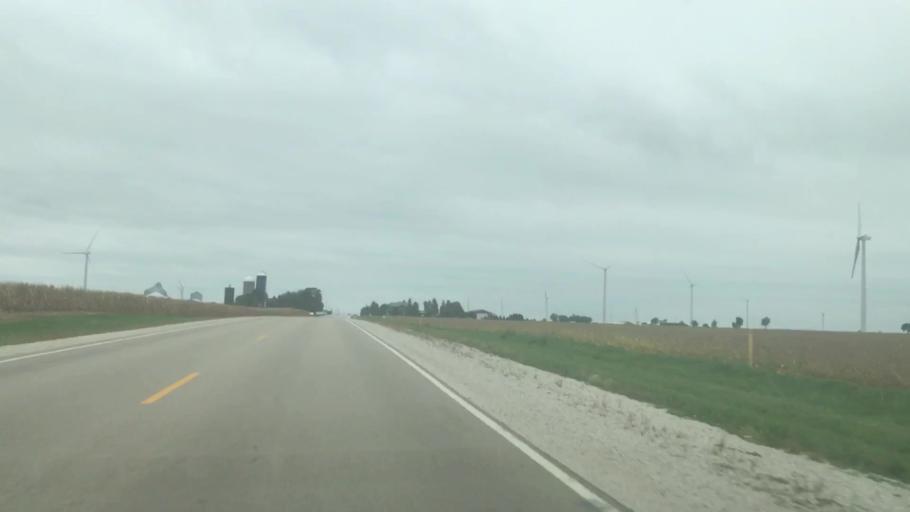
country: US
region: Wisconsin
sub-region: Fond du Lac County
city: Oakfield
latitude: 43.6318
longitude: -88.5418
